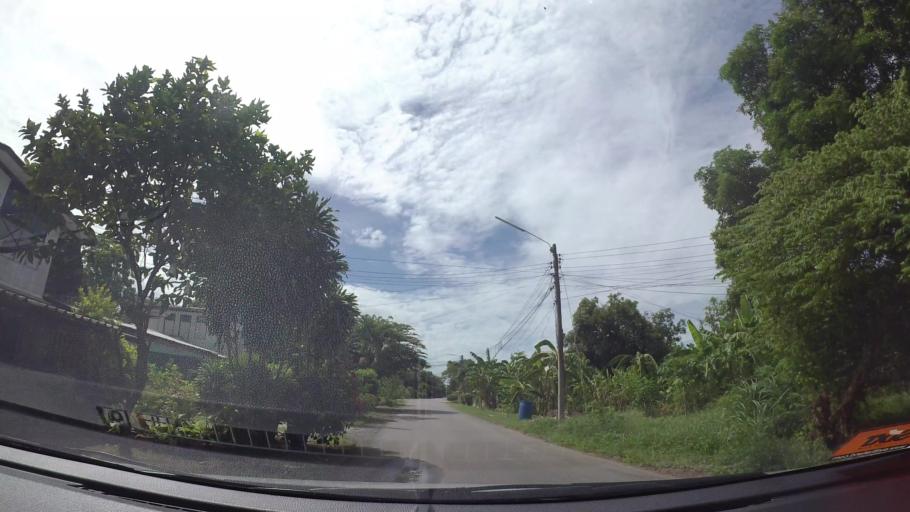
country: TH
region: Chon Buri
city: Sattahip
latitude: 12.6661
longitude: 100.9100
